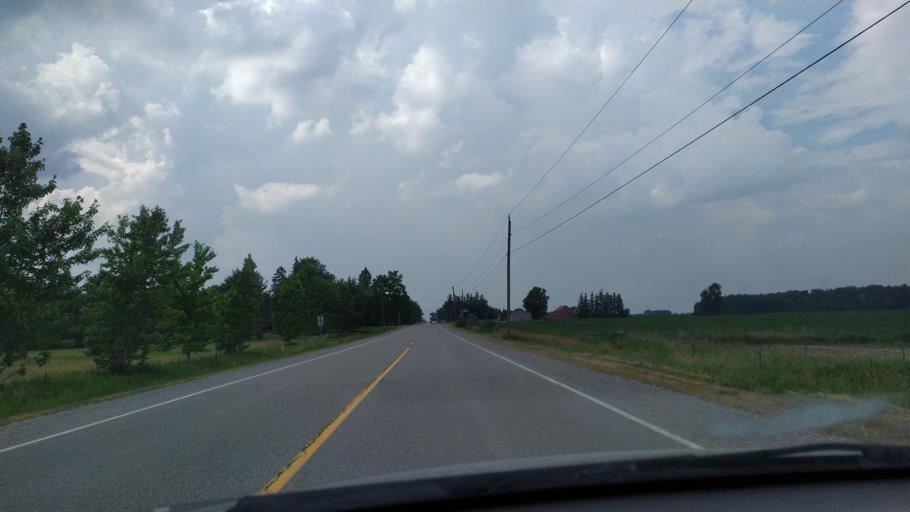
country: CA
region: Ontario
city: Dorchester
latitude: 43.1708
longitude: -81.1374
